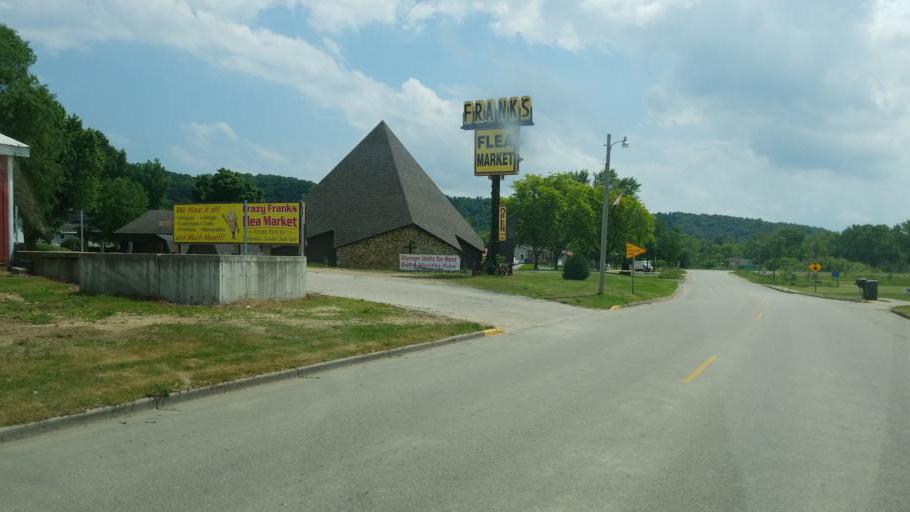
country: US
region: Wisconsin
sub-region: Vernon County
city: Viroqua
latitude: 43.4466
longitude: -90.7602
